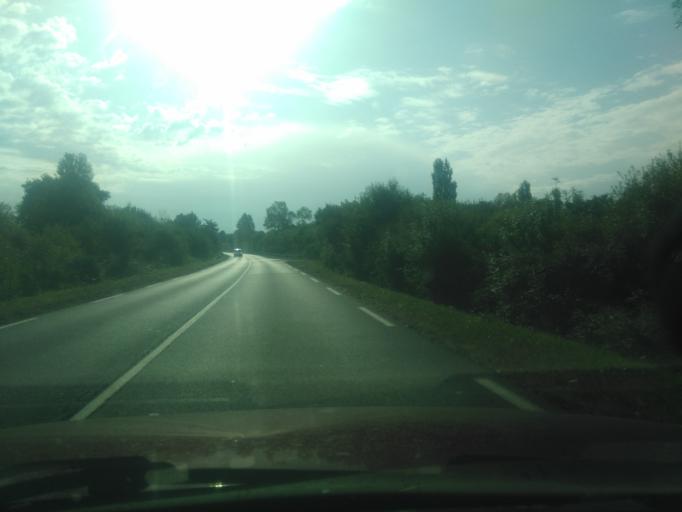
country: FR
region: Pays de la Loire
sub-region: Departement de la Vendee
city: Saint-Germain-de-Princay
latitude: 46.6770
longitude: -0.9866
